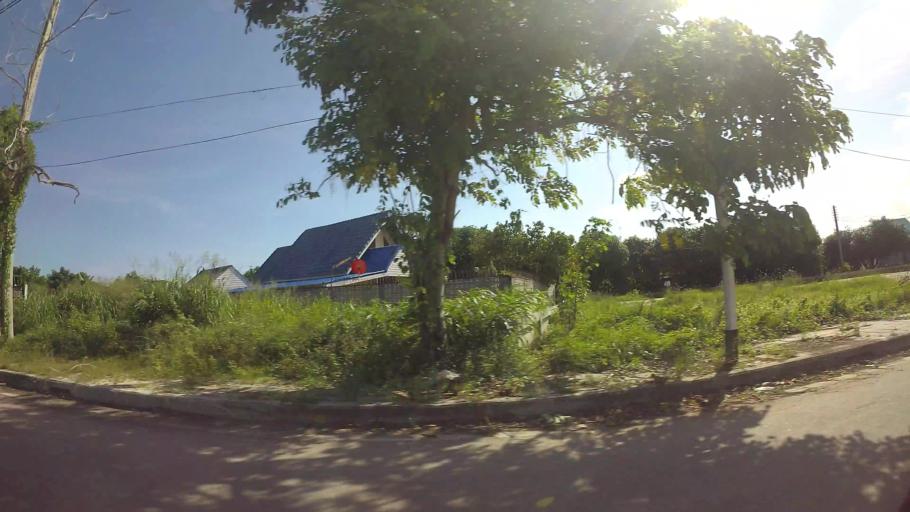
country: TH
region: Rayong
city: Rayong
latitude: 12.6765
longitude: 101.2945
